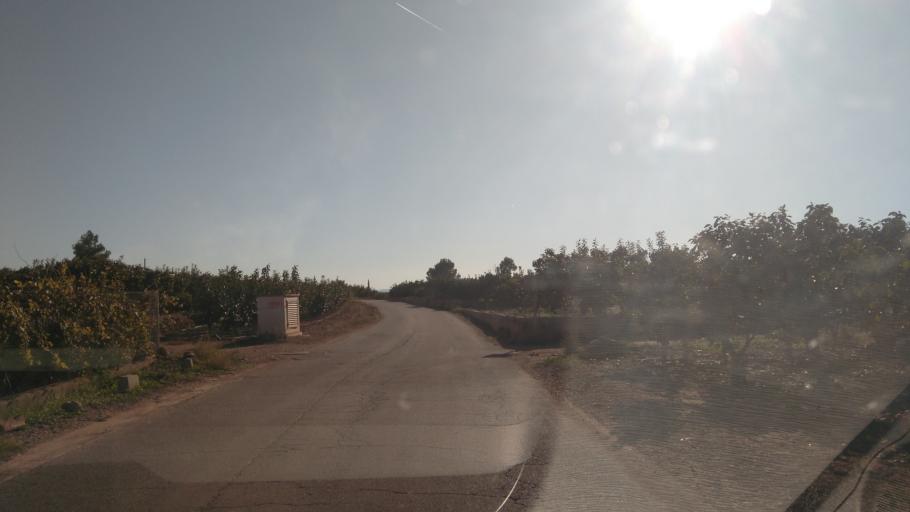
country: ES
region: Valencia
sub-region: Provincia de Valencia
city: Benimodo
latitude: 39.1820
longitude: -0.5303
